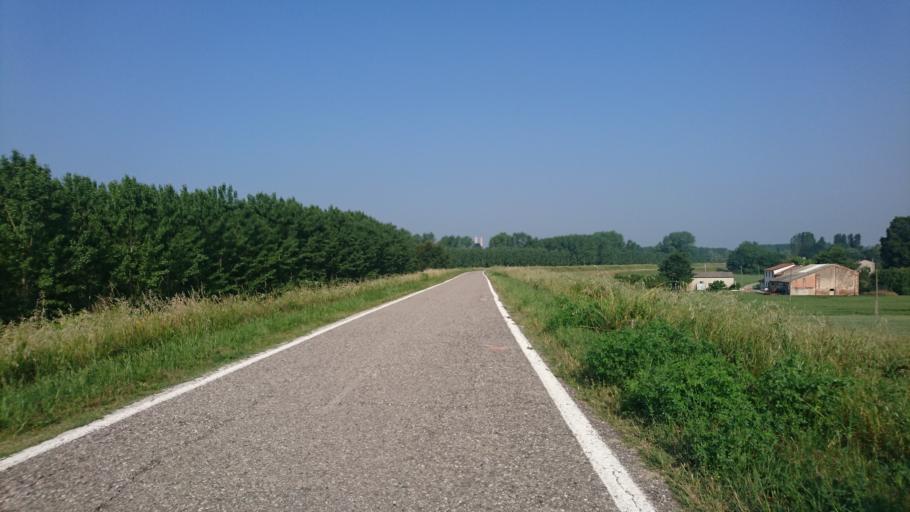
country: IT
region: Veneto
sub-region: Provincia di Rovigo
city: Castelnovo Bariano
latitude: 45.0215
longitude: 11.2779
